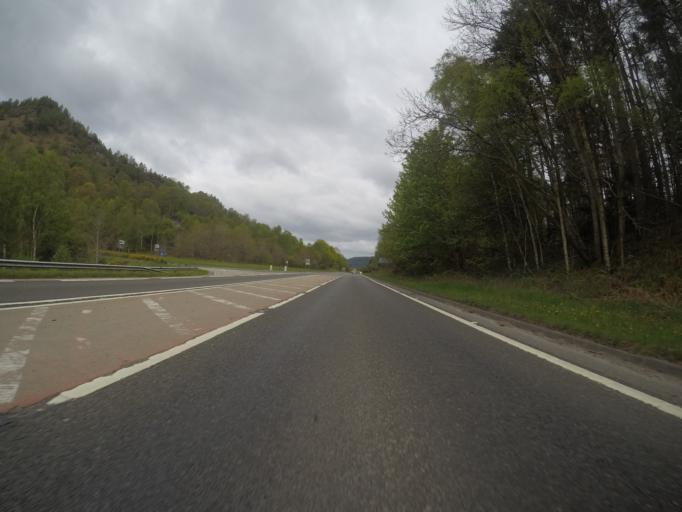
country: GB
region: Scotland
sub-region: Perth and Kinross
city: Bankfoot
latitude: 56.5498
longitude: -3.5616
